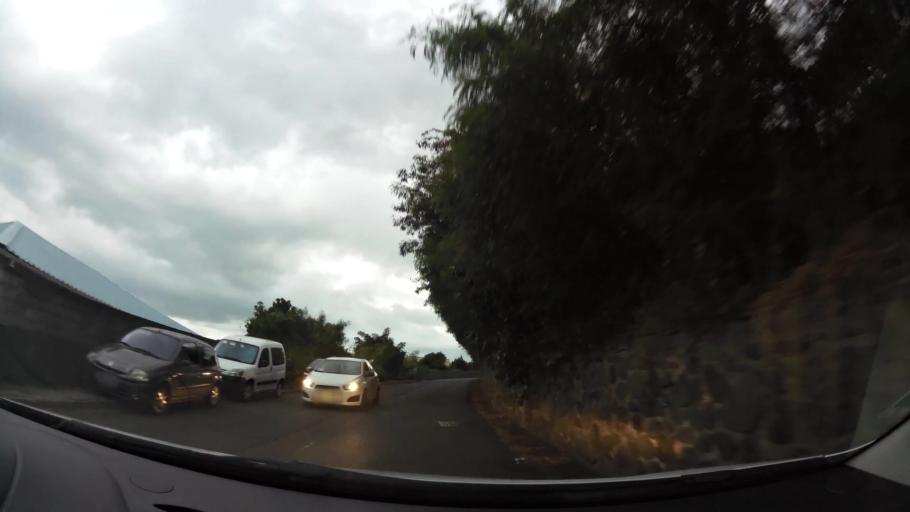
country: RE
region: Reunion
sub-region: Reunion
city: Saint-Denis
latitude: -20.9049
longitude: 55.4666
